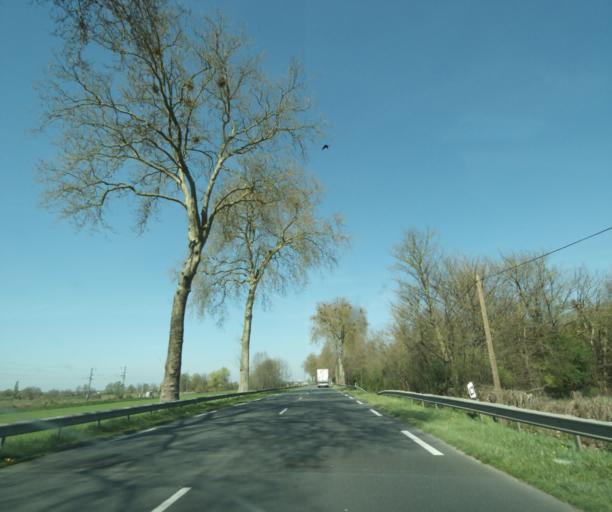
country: FR
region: Bourgogne
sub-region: Departement de la Nievre
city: Chantenay-Saint-Imbert
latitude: 46.6946
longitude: 3.2114
